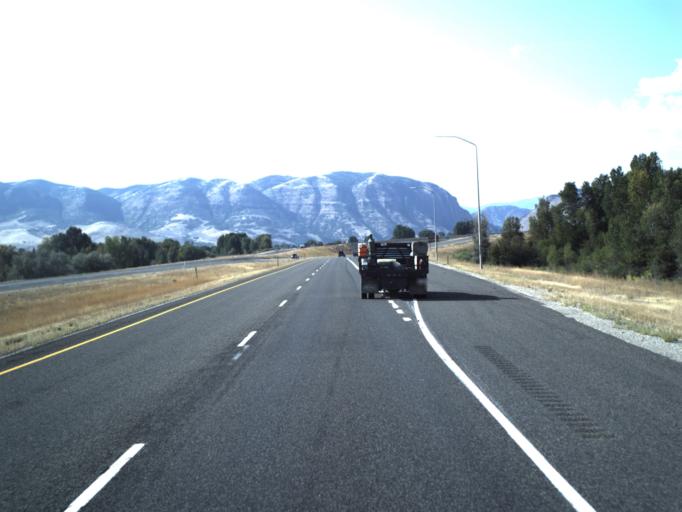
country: US
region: Utah
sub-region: Summit County
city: Coalville
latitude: 41.0127
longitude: -111.4856
